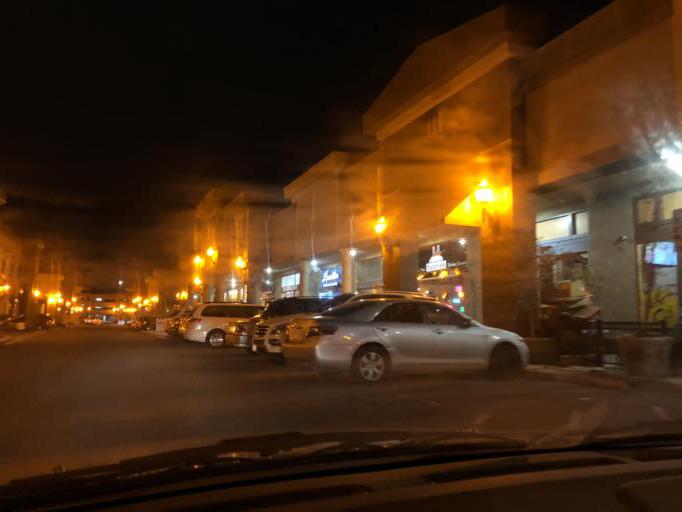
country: US
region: California
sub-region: Santa Clara County
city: San Jose
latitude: 37.3310
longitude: -121.8573
